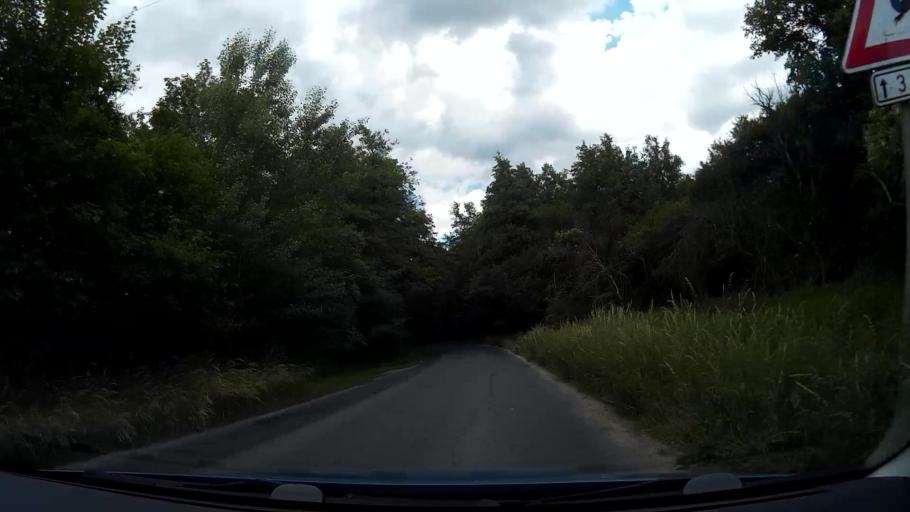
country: CZ
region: South Moravian
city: Orechov
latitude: 49.1217
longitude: 16.5263
